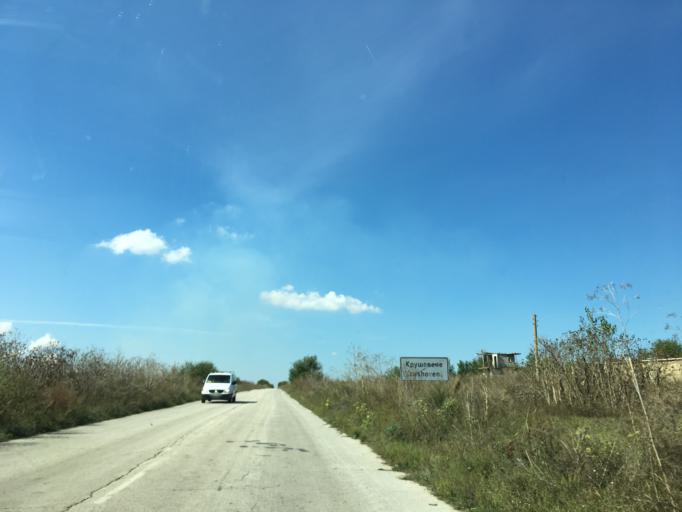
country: RO
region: Olt
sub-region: Comuna Orlea
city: Orlea
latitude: 43.6385
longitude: 24.3895
